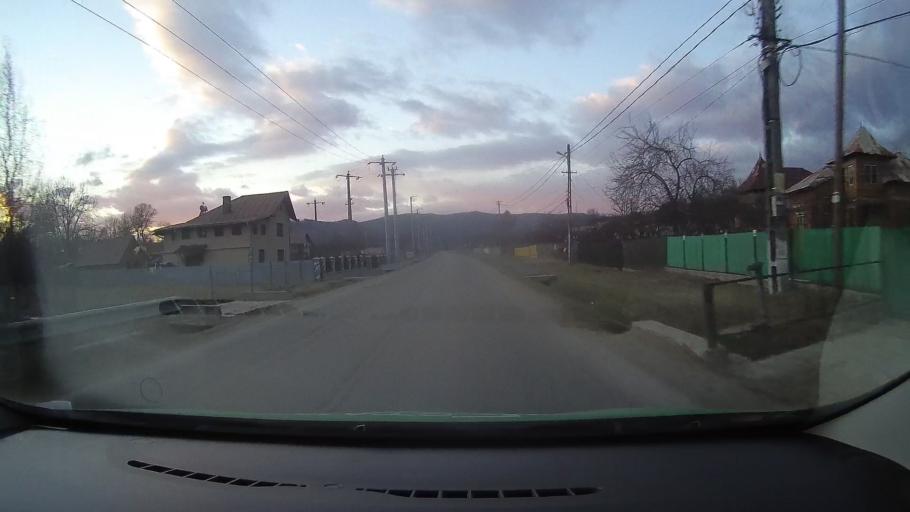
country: RO
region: Dambovita
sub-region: Comuna Valea Lunga
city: Valea Lunga-Cricov
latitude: 45.0639
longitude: 25.5874
